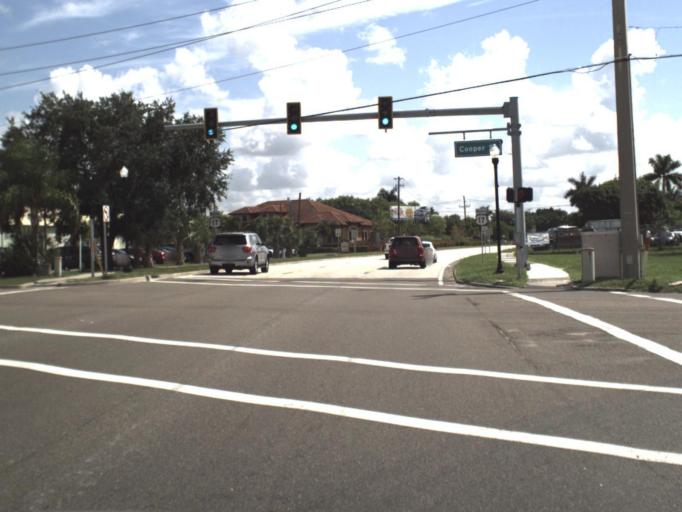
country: US
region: Florida
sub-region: Charlotte County
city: Punta Gorda
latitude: 26.9402
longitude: -82.0396
